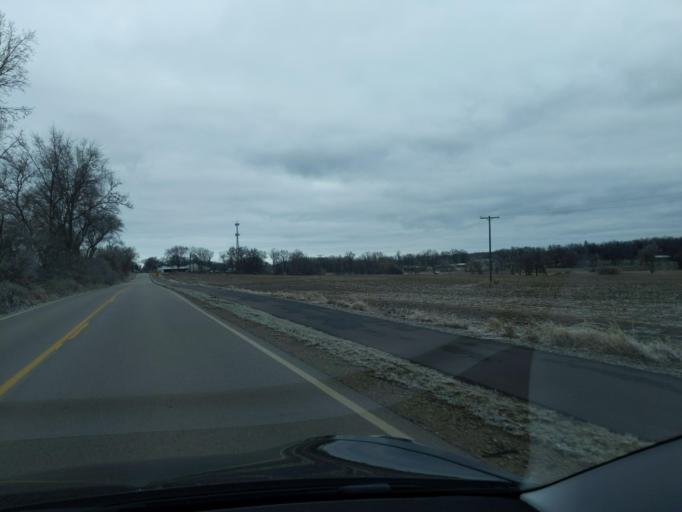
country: US
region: Michigan
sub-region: Jackson County
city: Spring Arbor
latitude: 42.1911
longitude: -84.5534
